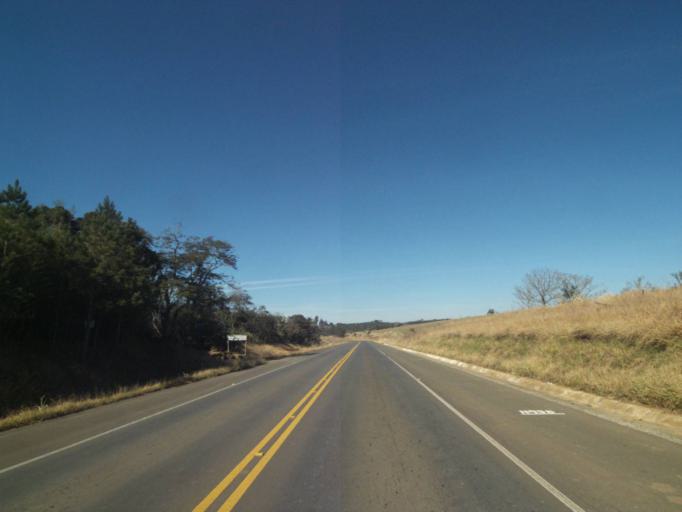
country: BR
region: Parana
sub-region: Tibagi
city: Tibagi
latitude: -24.7682
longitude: -50.4678
